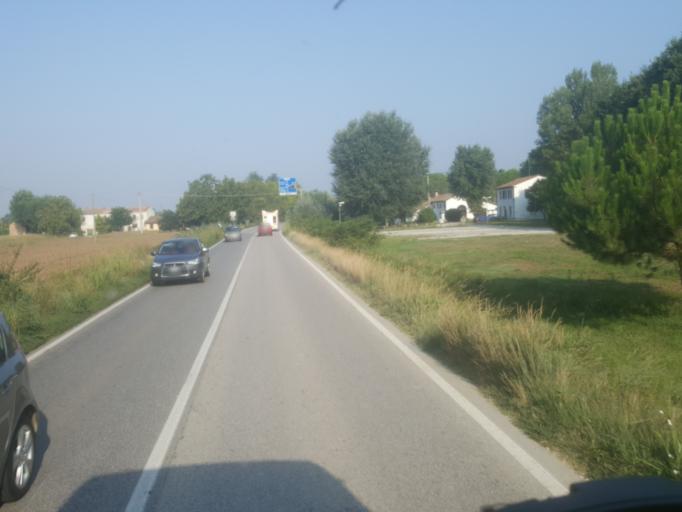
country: IT
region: Emilia-Romagna
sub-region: Provincia di Ravenna
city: Alfonsine
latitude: 44.4951
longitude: 12.0595
